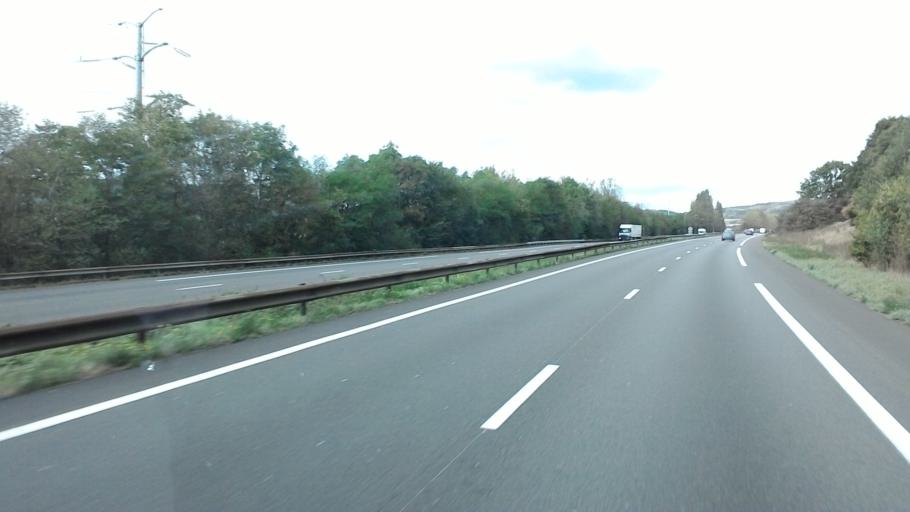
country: FR
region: Lorraine
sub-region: Departement de Meurthe-et-Moselle
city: Frouard
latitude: 48.7683
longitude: 6.1439
